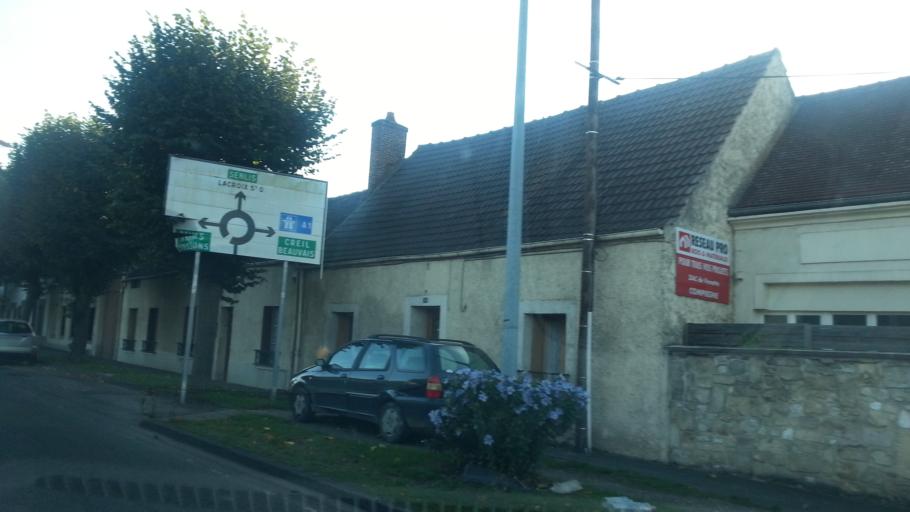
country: FR
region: Picardie
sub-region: Departement de l'Oise
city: Venette
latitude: 49.3946
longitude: 2.8034
